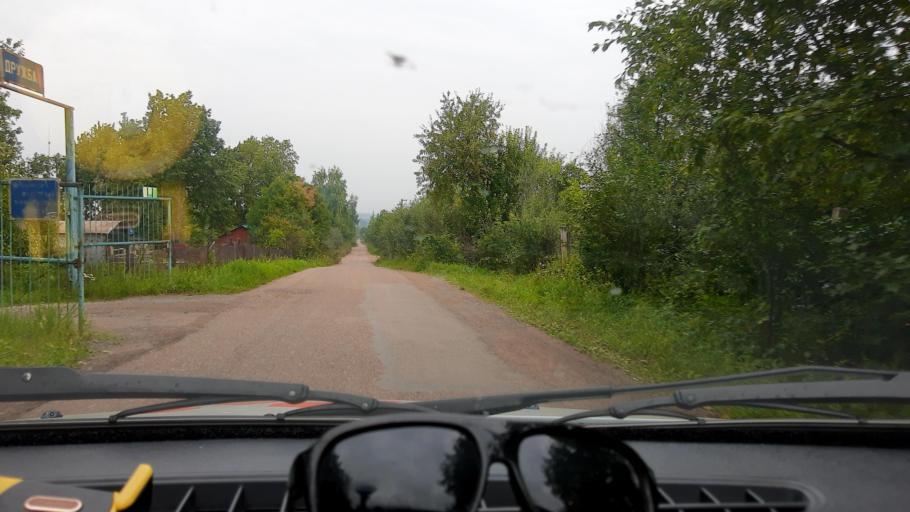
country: RU
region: Bashkortostan
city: Asanovo
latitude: 54.9824
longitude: 55.6108
